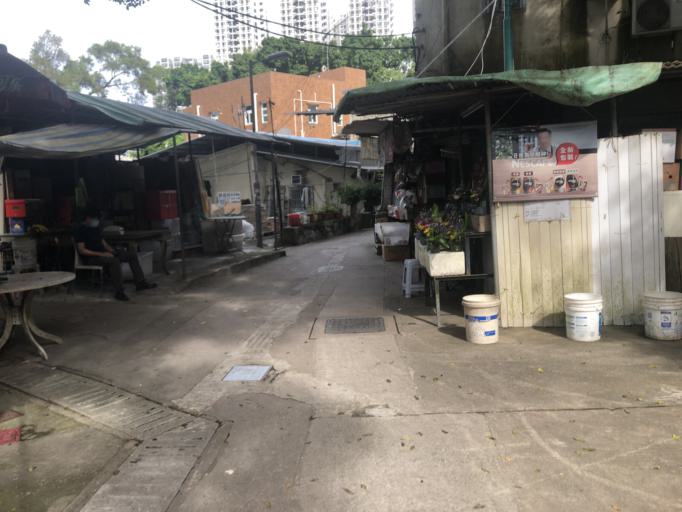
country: HK
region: Sha Tin
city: Sha Tin
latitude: 22.3846
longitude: 114.1870
